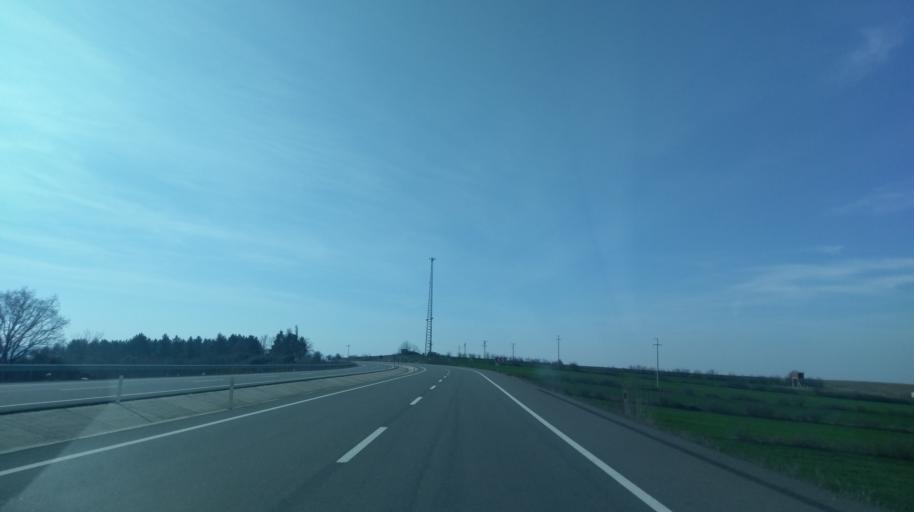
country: TR
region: Edirne
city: Hamidiye
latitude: 41.0796
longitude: 26.6389
